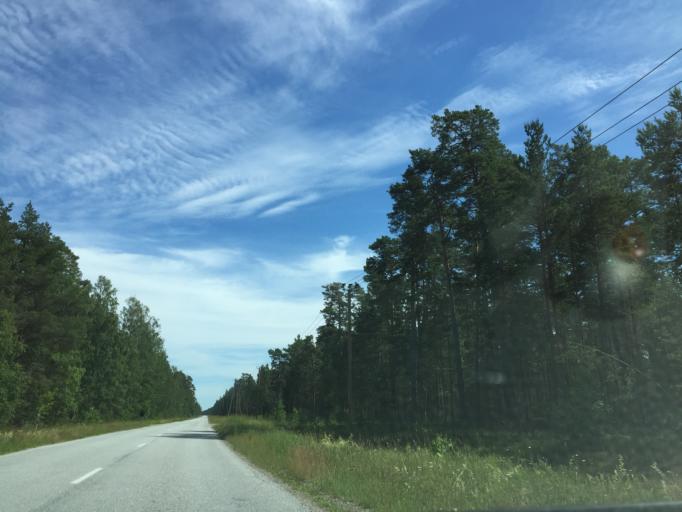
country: LV
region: Rojas
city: Roja
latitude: 57.5695
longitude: 22.6460
